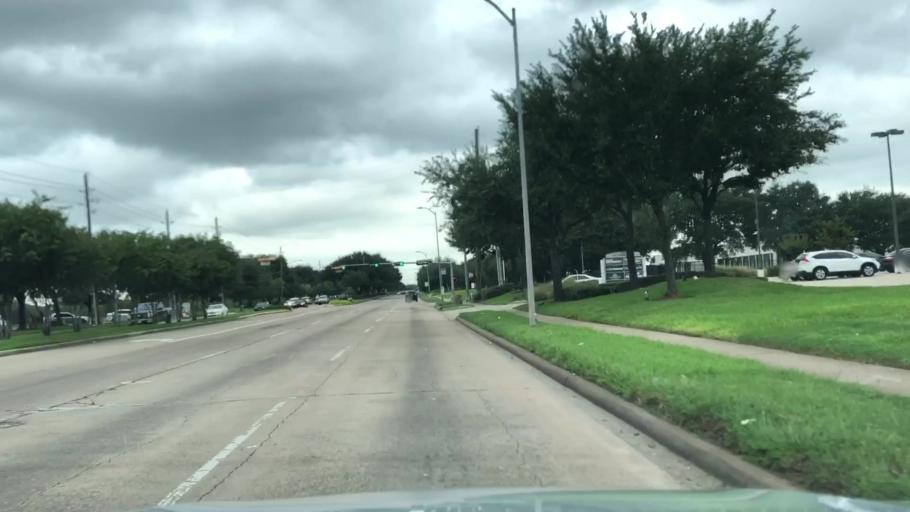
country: US
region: Texas
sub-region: Fort Bend County
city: Meadows Place
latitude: 29.7045
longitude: -95.5593
